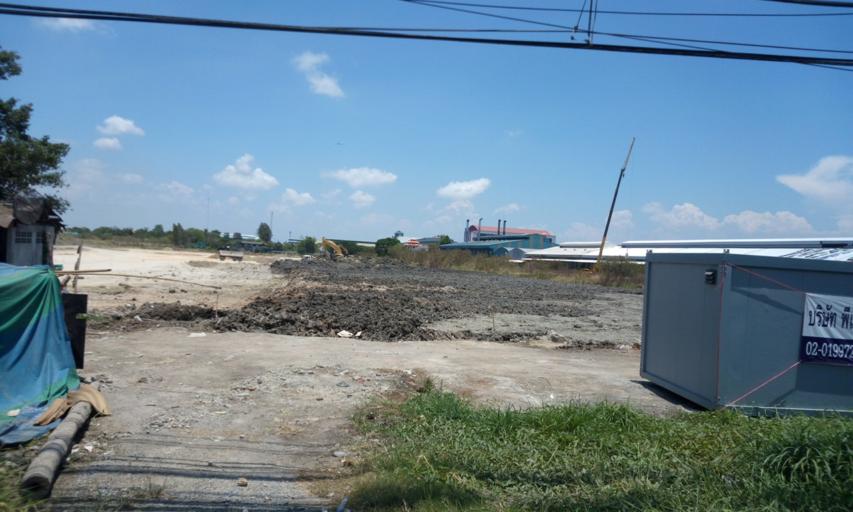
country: TH
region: Bangkok
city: Bang Na
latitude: 13.6221
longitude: 100.7053
